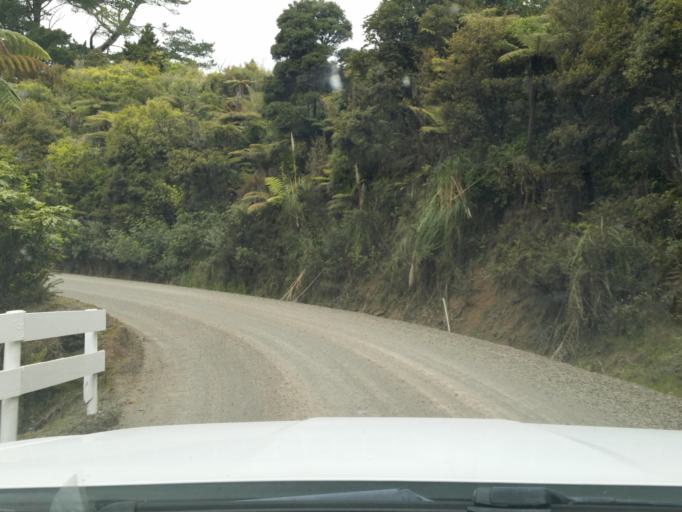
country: NZ
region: Northland
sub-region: Kaipara District
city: Dargaville
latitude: -35.7133
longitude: 173.6313
